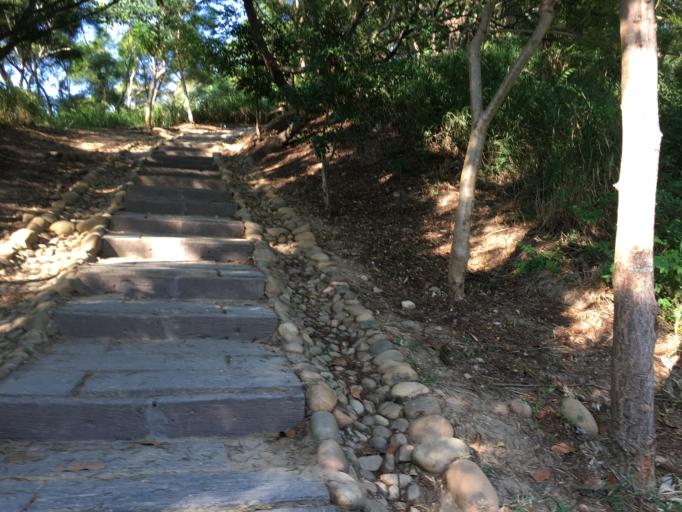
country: TW
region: Taiwan
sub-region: Changhua
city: Chang-hua
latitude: 24.1498
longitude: 120.5657
